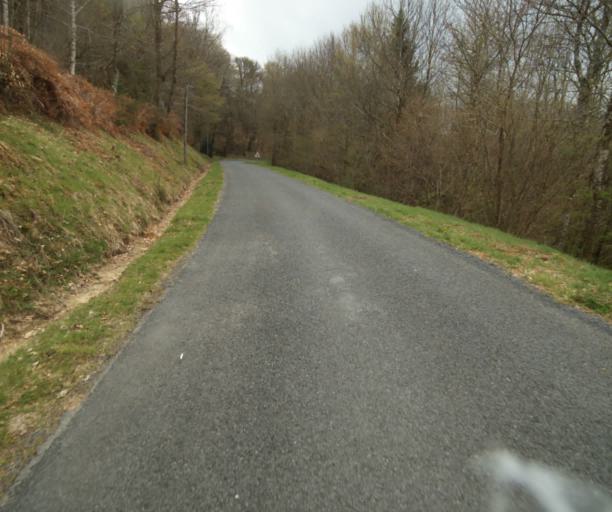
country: FR
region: Limousin
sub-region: Departement de la Correze
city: Laguenne
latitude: 45.2491
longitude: 1.8882
